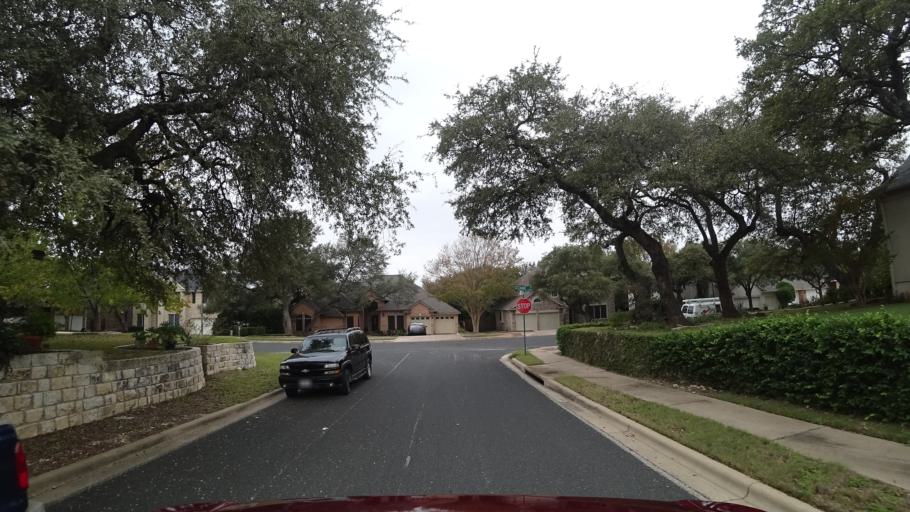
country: US
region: Texas
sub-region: Williamson County
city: Anderson Mill
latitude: 30.4494
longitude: -97.8204
